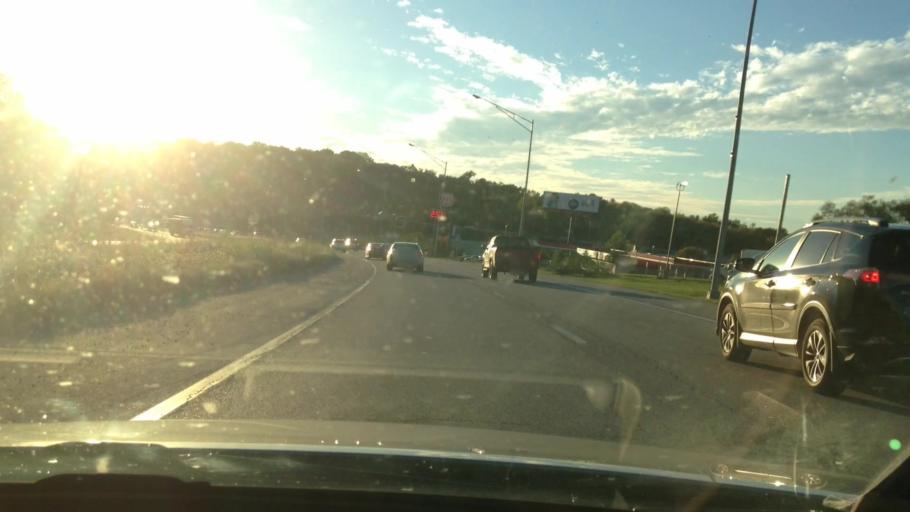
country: US
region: Missouri
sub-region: Clay County
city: Claycomo
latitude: 39.1602
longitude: -94.4921
